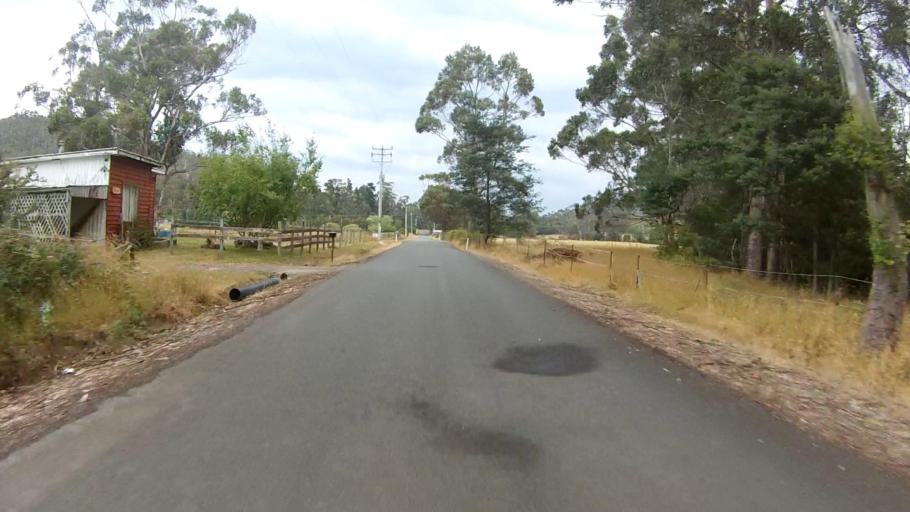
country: AU
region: Tasmania
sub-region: Huon Valley
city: Cygnet
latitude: -43.2374
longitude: 147.1553
